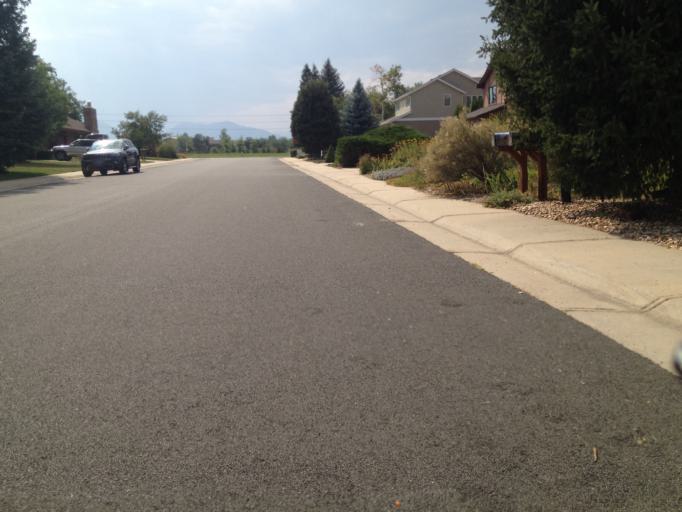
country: US
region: Colorado
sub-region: Boulder County
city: Louisville
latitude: 39.9887
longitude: -105.1530
